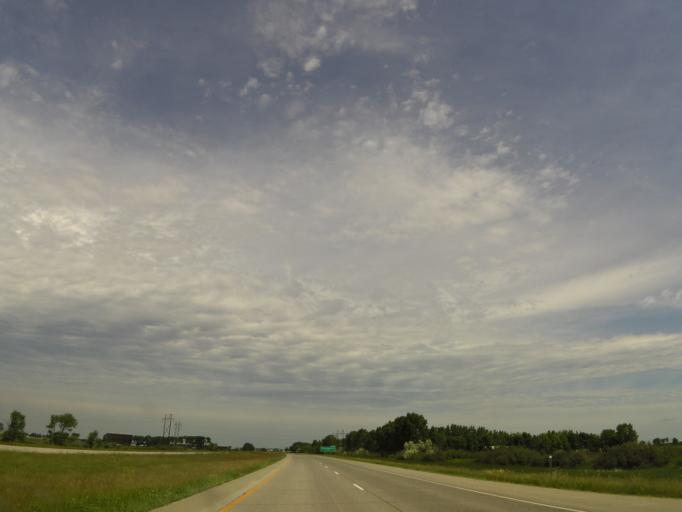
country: US
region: North Dakota
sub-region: Grand Forks County
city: Grand Forks
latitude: 47.9673
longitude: -97.0932
